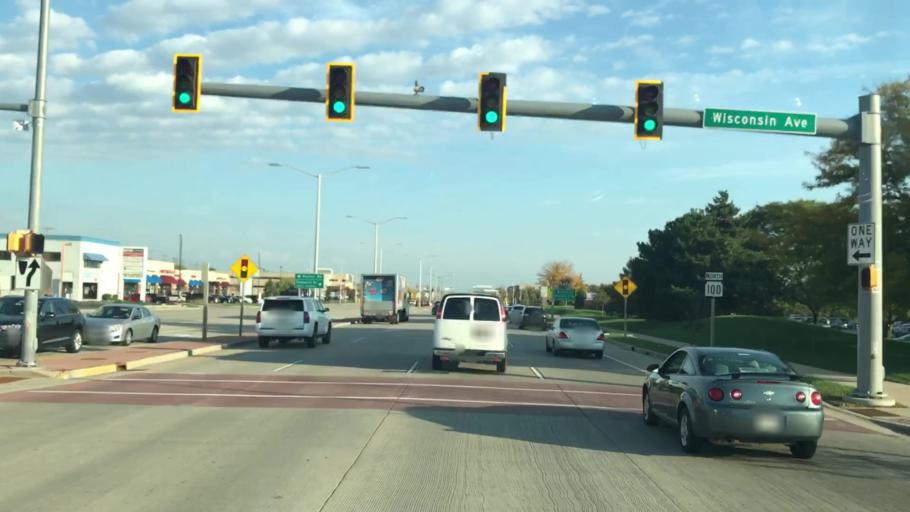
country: US
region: Wisconsin
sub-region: Waukesha County
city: Elm Grove
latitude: 43.0384
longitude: -88.0470
